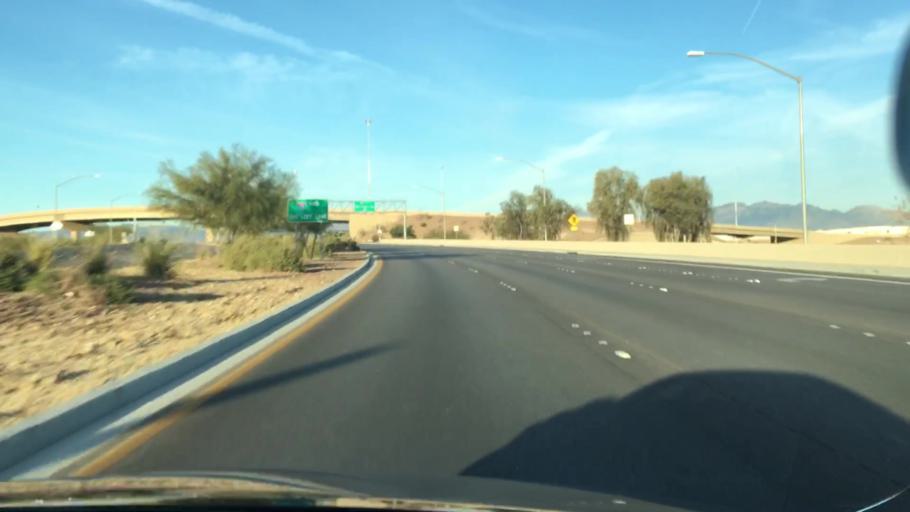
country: US
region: Nevada
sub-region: Clark County
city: Paradise
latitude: 36.0433
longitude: -115.1769
